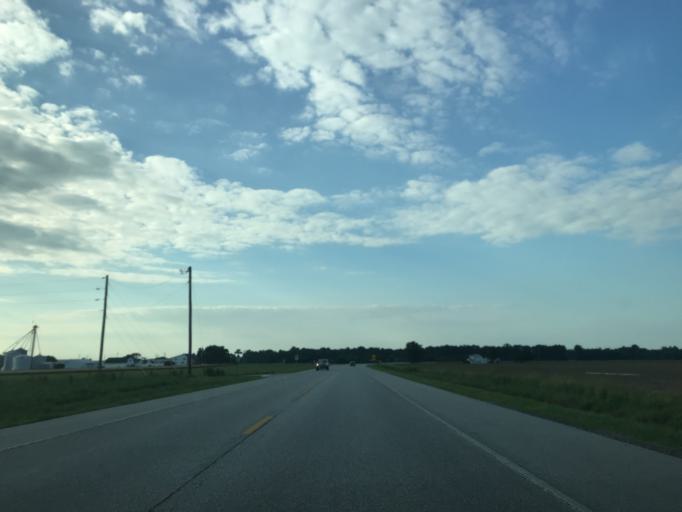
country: US
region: Maryland
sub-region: Caroline County
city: Federalsburg
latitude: 38.7432
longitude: -75.7935
